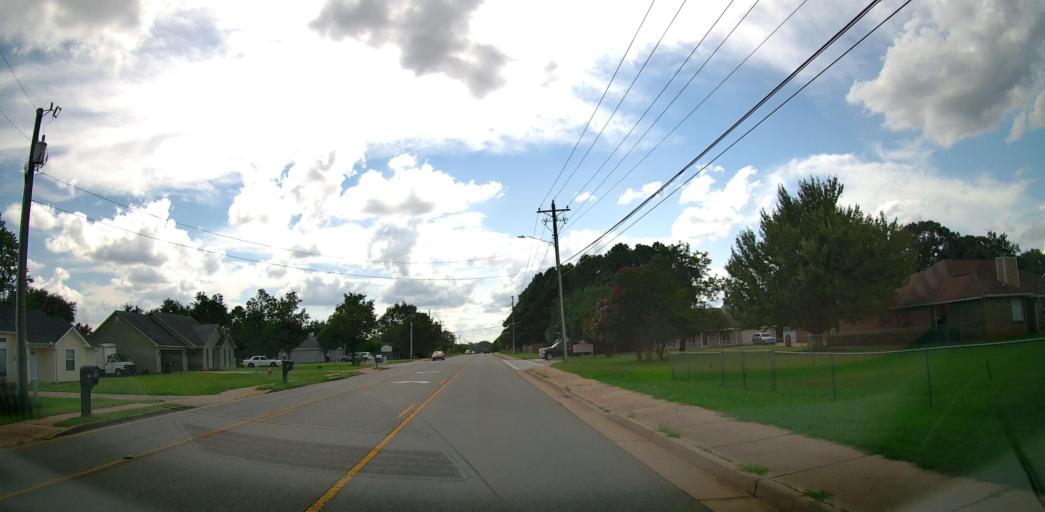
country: US
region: Georgia
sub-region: Houston County
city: Centerville
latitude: 32.5710
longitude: -83.6803
